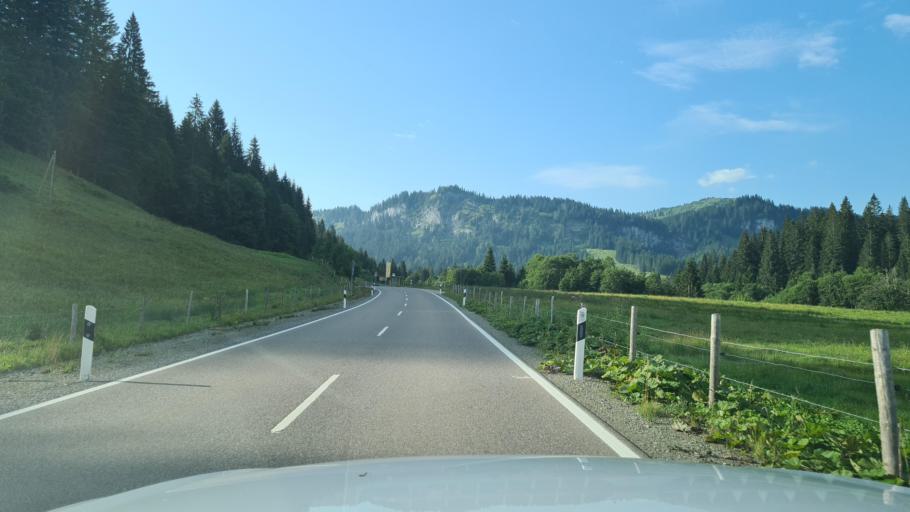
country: DE
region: Bavaria
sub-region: Swabia
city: Balderschwang
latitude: 47.4449
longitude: 10.1366
